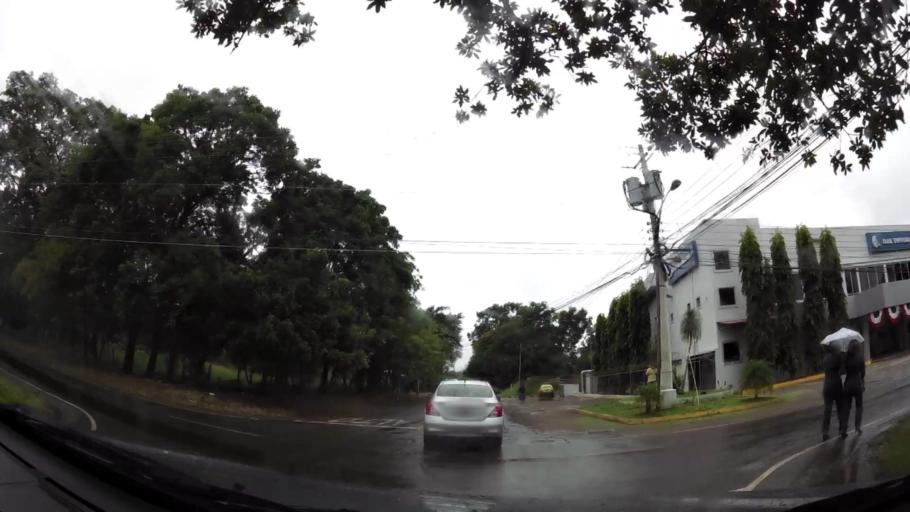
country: PA
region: Chiriqui
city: David
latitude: 8.4309
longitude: -82.4382
